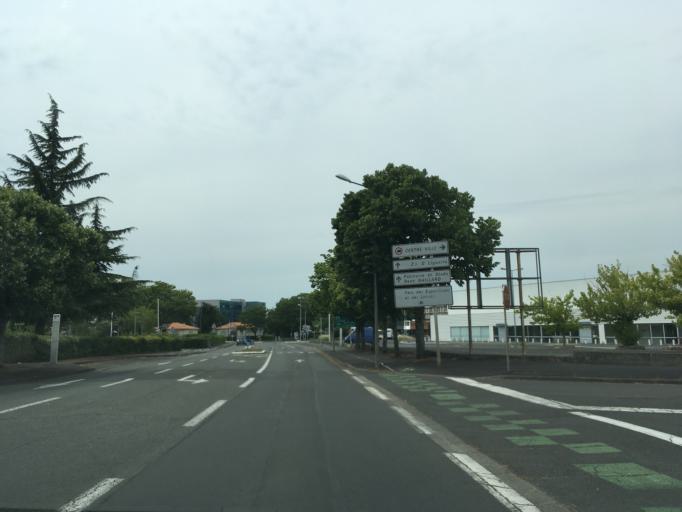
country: FR
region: Poitou-Charentes
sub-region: Departement des Deux-Sevres
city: Niort
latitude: 46.3113
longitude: -0.4767
